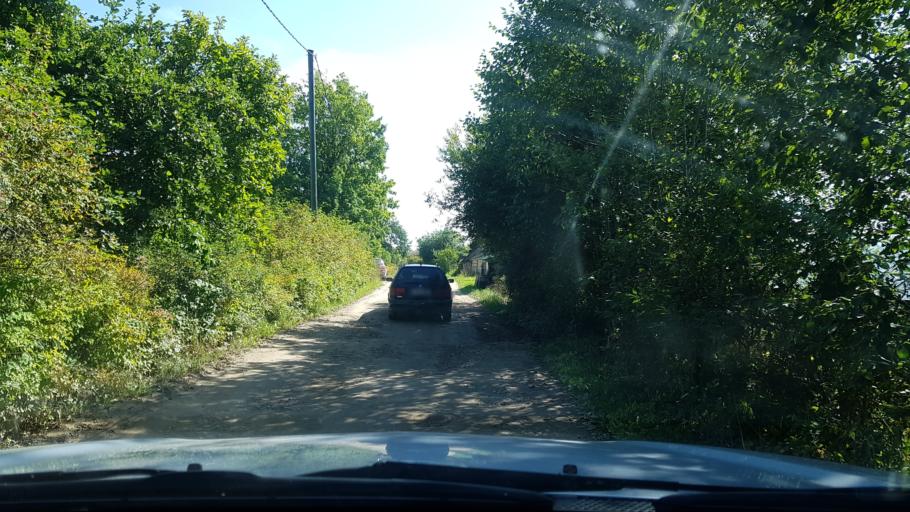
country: EE
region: Ida-Virumaa
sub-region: Sillamaee linn
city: Sillamae
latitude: 59.3752
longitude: 27.7816
